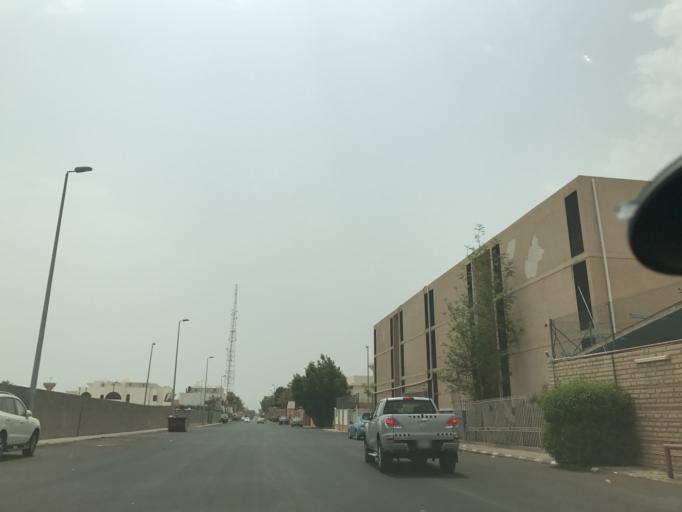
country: SA
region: Makkah
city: Jeddah
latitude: 21.5592
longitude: 39.1668
